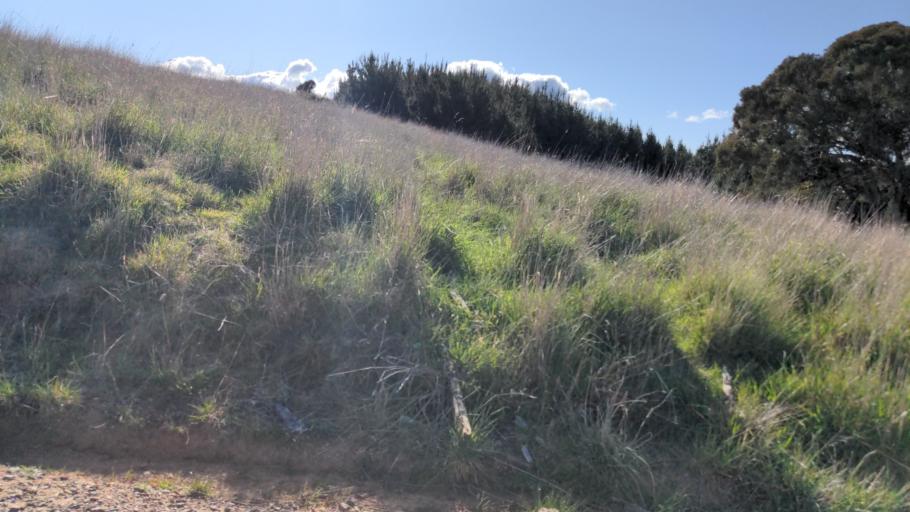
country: AU
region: New South Wales
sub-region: Blayney
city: Blayney
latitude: -33.4163
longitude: 149.3147
